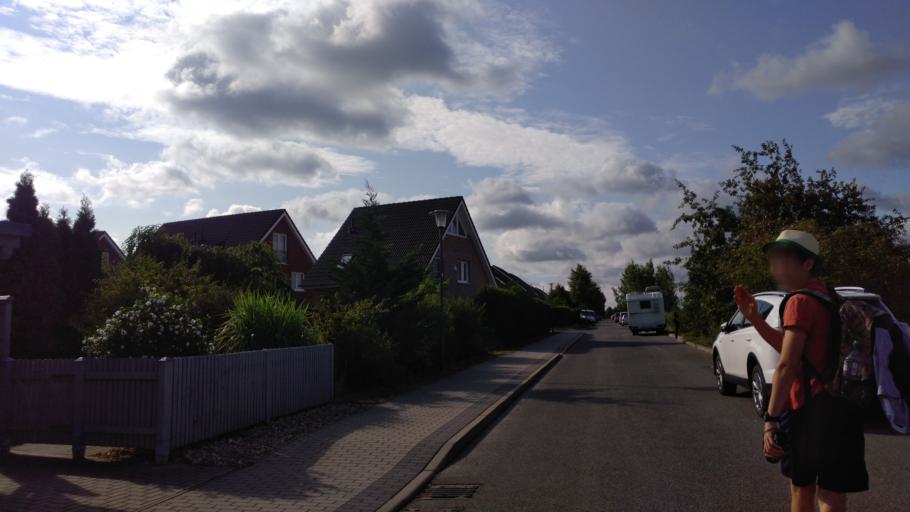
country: DE
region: Brandenburg
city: Grossbeeren
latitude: 52.3669
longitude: 13.3050
